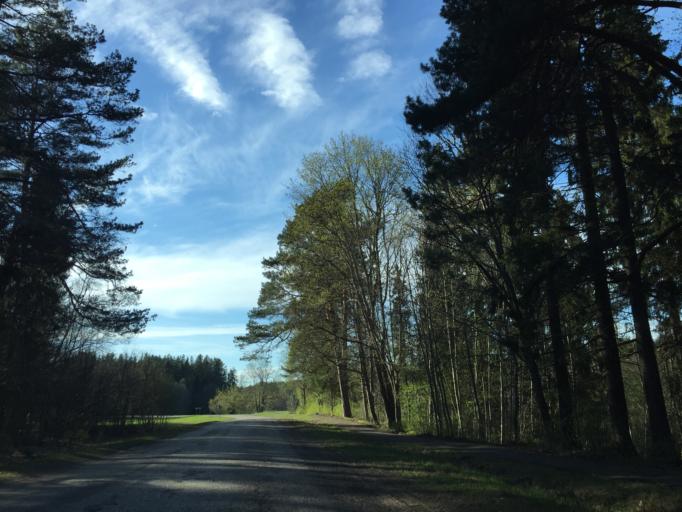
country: LV
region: Valkas Rajons
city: Valka
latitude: 57.7920
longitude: 25.9800
